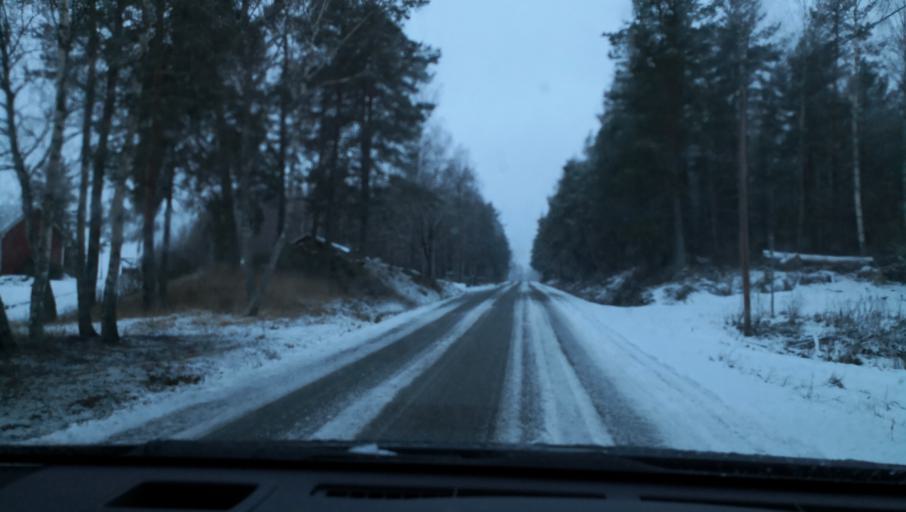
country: SE
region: Vaestmanland
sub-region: Kopings Kommun
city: Koping
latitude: 59.5759
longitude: 15.9572
